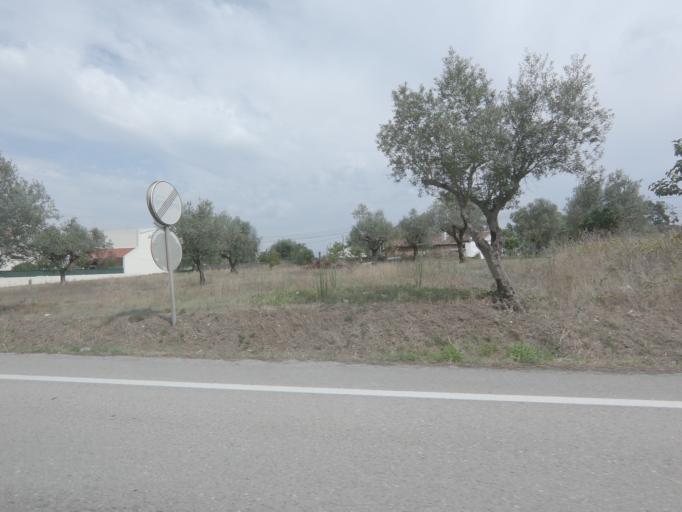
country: PT
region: Leiria
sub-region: Pombal
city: Pombal
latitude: 39.8628
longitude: -8.6979
